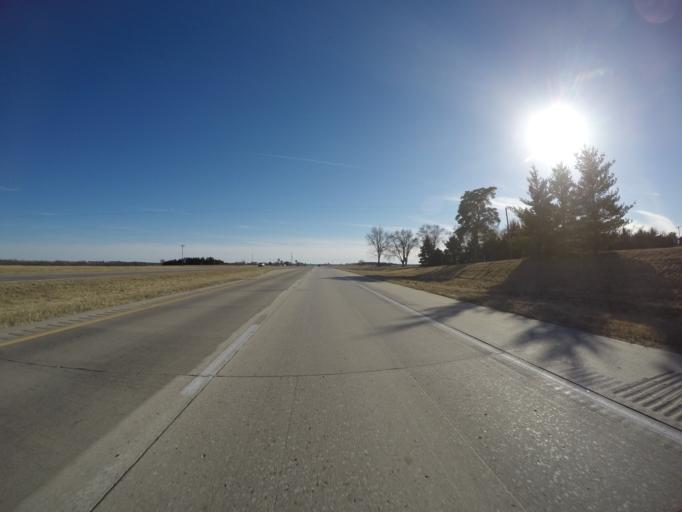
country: US
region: Nebraska
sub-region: Gage County
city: Beatrice
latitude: 40.3249
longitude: -96.7471
